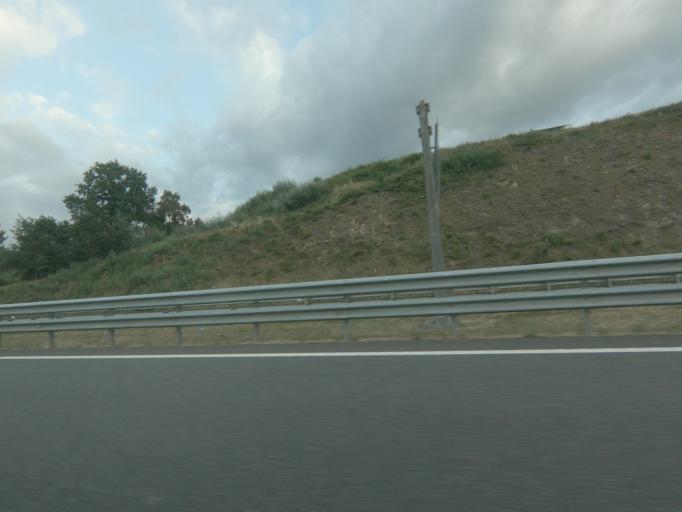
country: ES
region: Galicia
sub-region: Provincia de Ourense
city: Punxin
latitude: 42.3410
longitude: -7.9984
